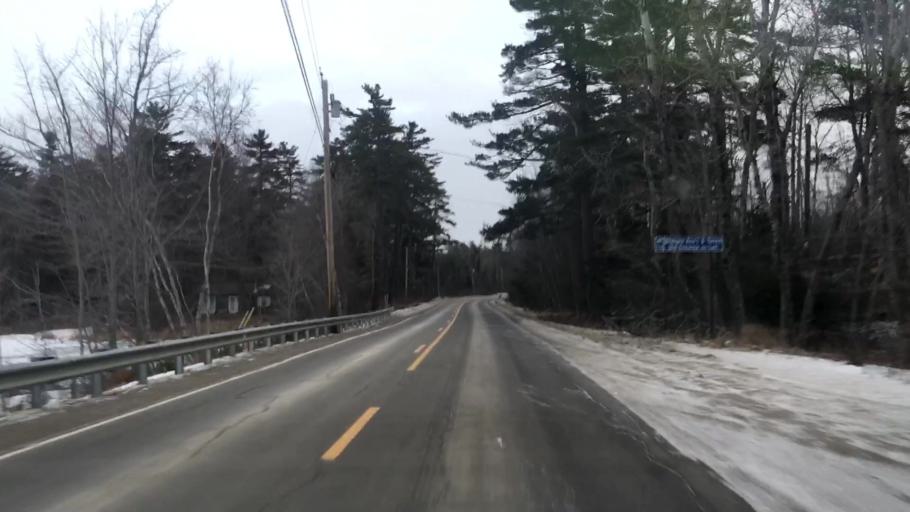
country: US
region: Maine
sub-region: Hancock County
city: Ellsworth
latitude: 44.6156
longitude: -68.3858
